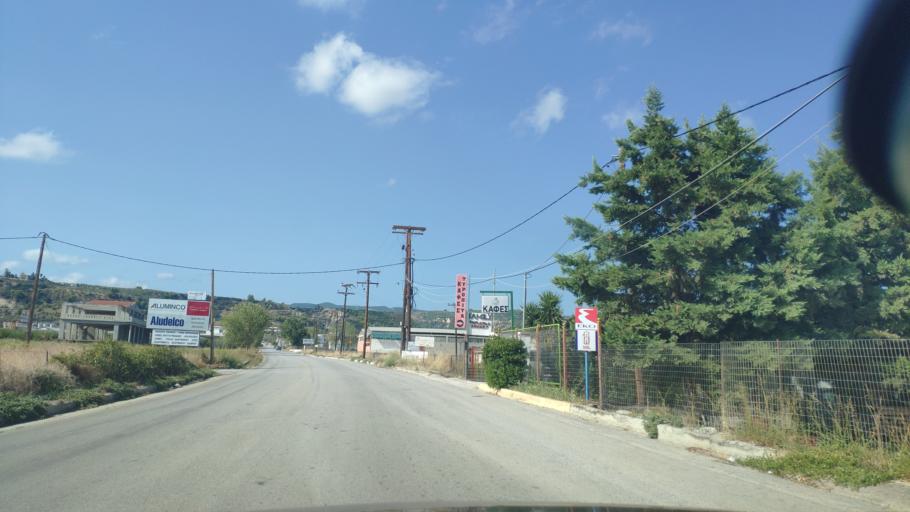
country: GR
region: Peloponnese
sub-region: Nomos Korinthias
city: Pasion
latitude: 38.0046
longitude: 22.7265
